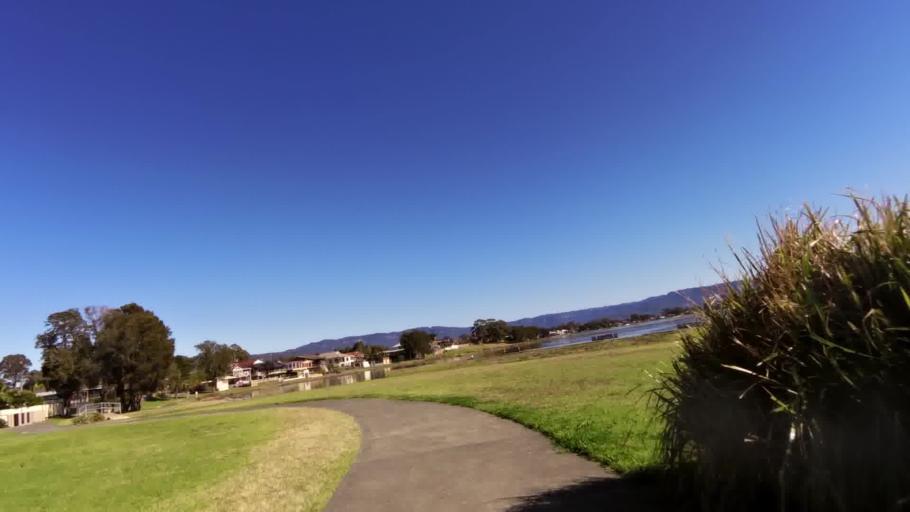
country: AU
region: New South Wales
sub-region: Shellharbour
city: Barrack Heights
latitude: -34.5558
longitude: 150.8337
